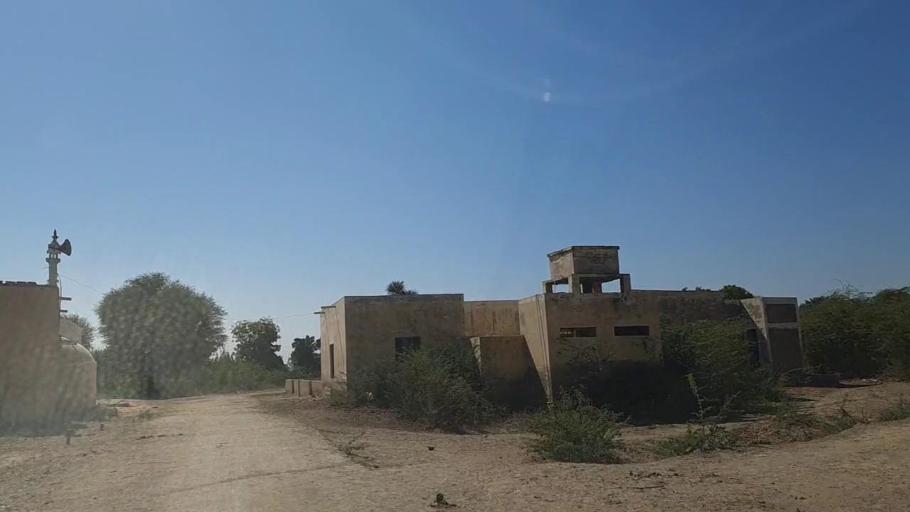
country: PK
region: Sindh
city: Samaro
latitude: 25.3438
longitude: 69.4865
